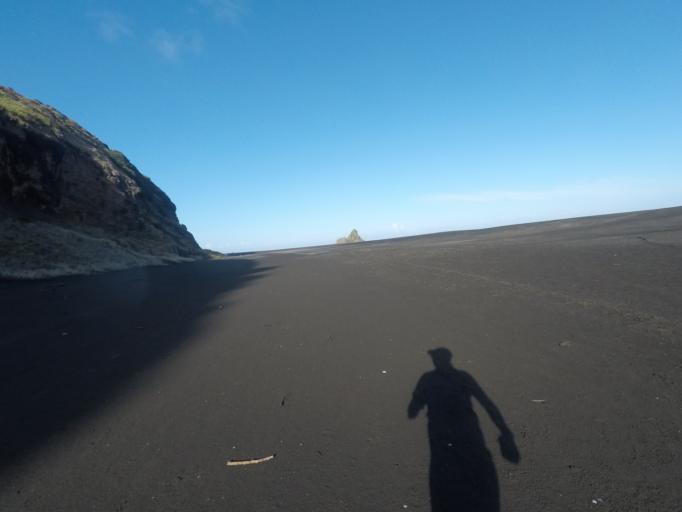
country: NZ
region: Auckland
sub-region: Auckland
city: Muriwai Beach
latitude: -36.9911
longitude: 174.4745
